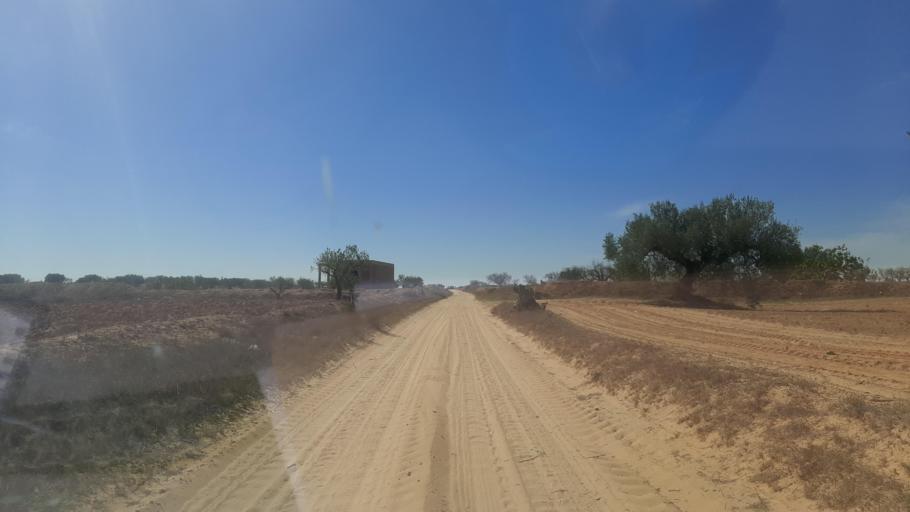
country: TN
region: Safaqis
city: Sfax
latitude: 34.8159
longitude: 10.5489
